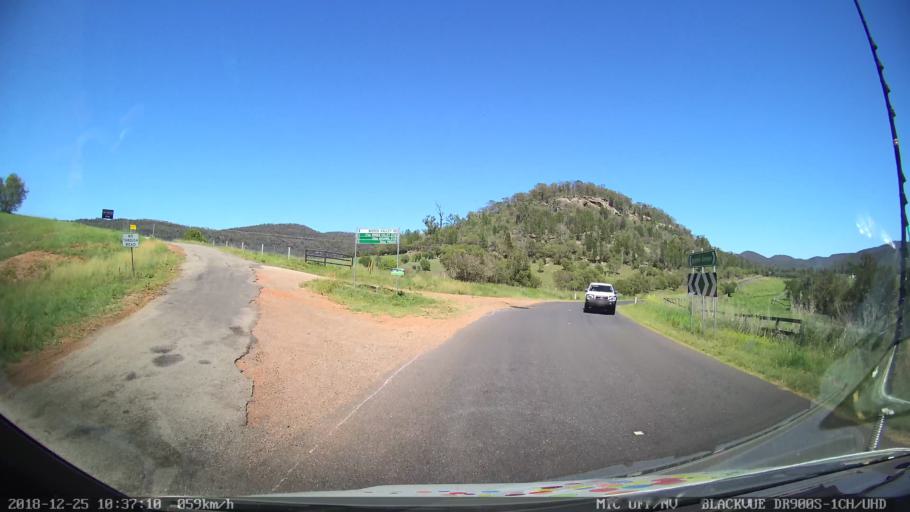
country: AU
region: New South Wales
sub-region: Upper Hunter Shire
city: Merriwa
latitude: -32.4102
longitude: 150.3808
